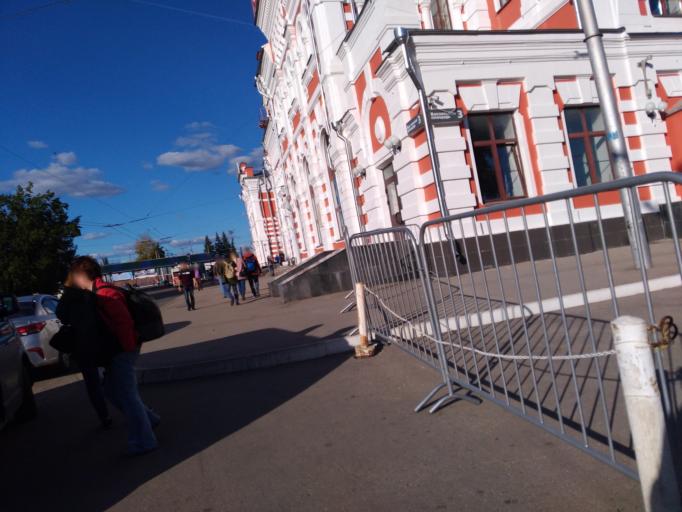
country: RU
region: Kaluga
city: Kaluga
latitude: 54.5331
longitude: 36.2781
